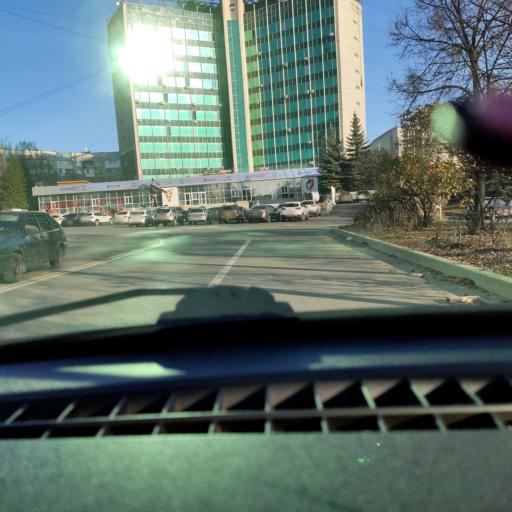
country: RU
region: Bashkortostan
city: Ufa
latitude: 54.8136
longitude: 56.0650
